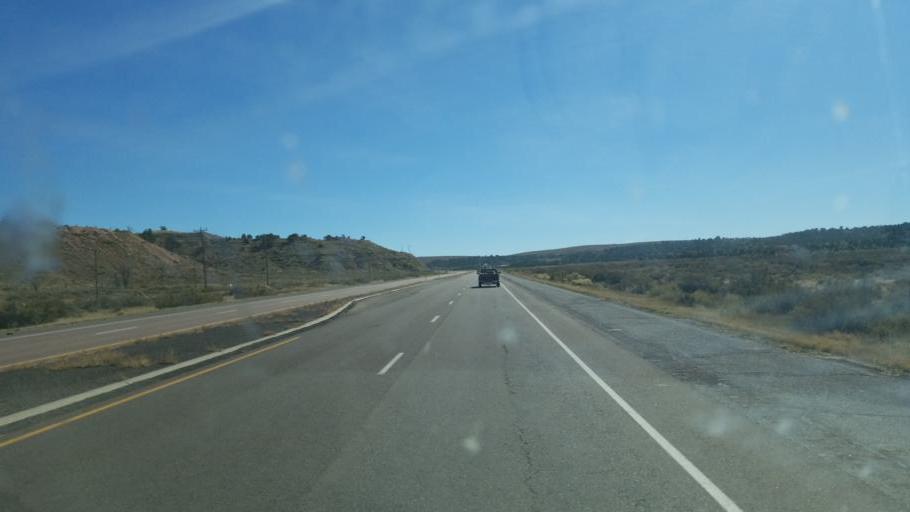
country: US
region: Arizona
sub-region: Apache County
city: Window Rock
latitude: 35.6426
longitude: -109.0221
